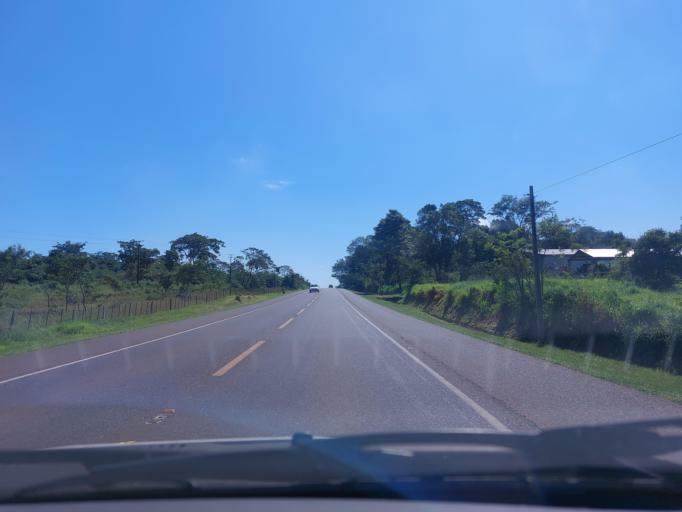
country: PY
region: San Pedro
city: Guayaybi
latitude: -24.6294
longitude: -56.4764
